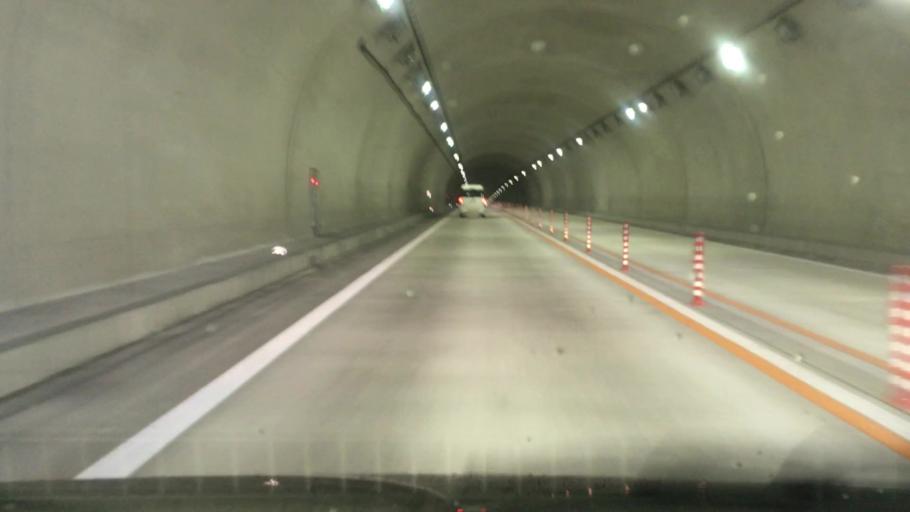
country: JP
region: Hyogo
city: Toyooka
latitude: 35.4432
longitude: 134.7670
